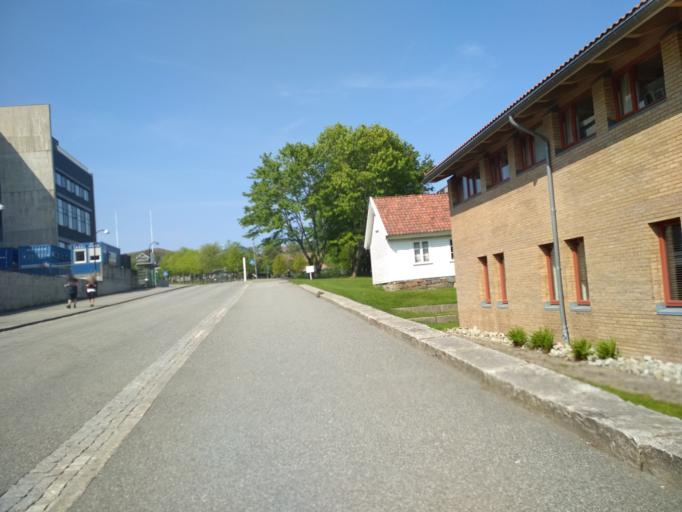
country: NO
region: Rogaland
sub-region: Stavanger
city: Stavanger
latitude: 58.9368
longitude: 5.6982
